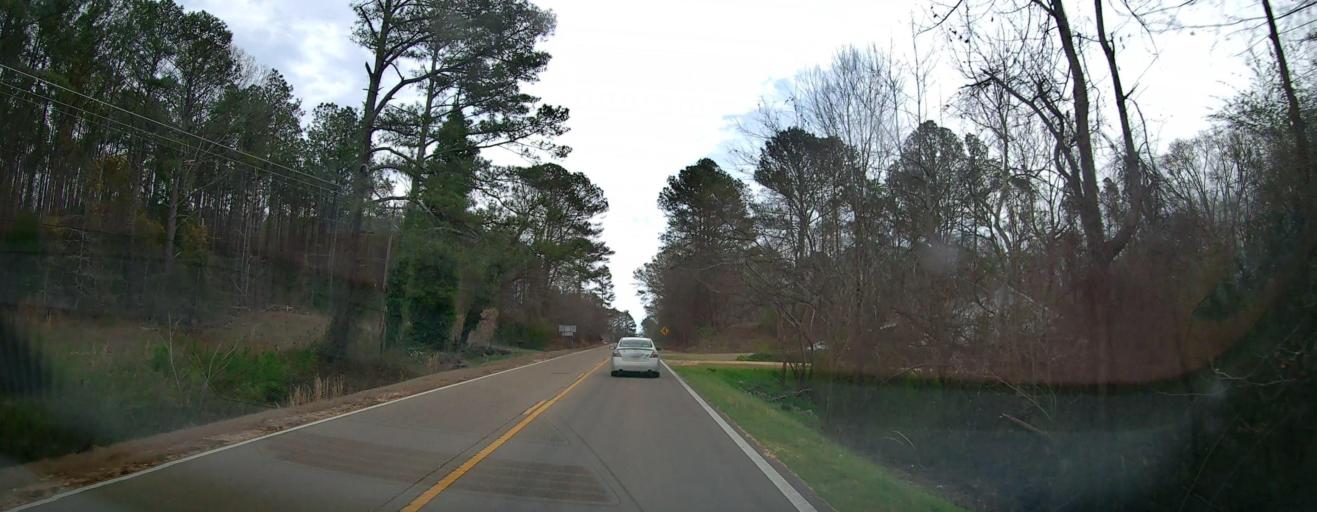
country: US
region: Mississippi
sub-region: Itawamba County
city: Fulton
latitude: 34.2751
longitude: -88.3502
